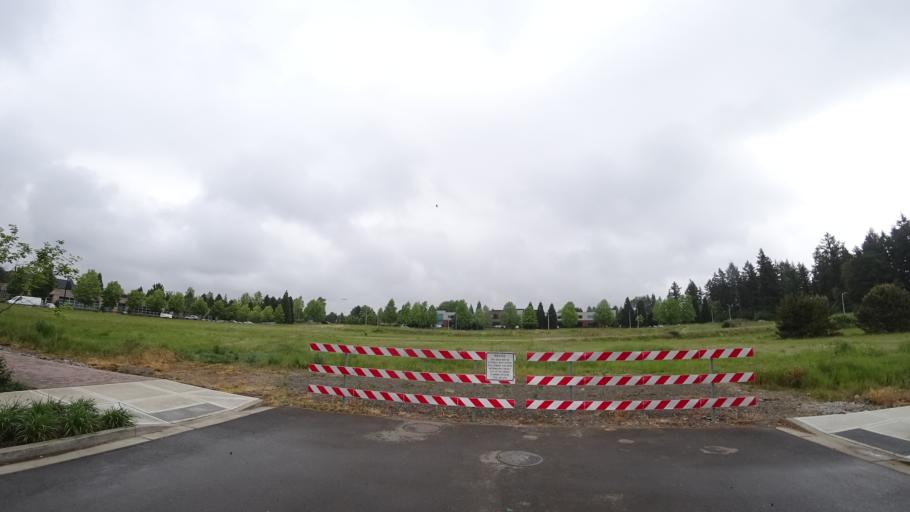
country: US
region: Oregon
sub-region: Washington County
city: Rockcreek
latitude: 45.5280
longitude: -122.8865
